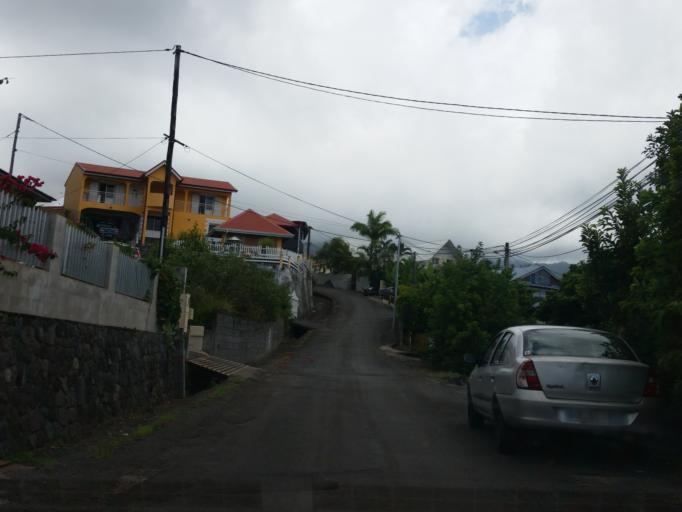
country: RE
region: Reunion
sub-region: Reunion
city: L'Entre-Deux
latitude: -21.2435
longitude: 55.4793
